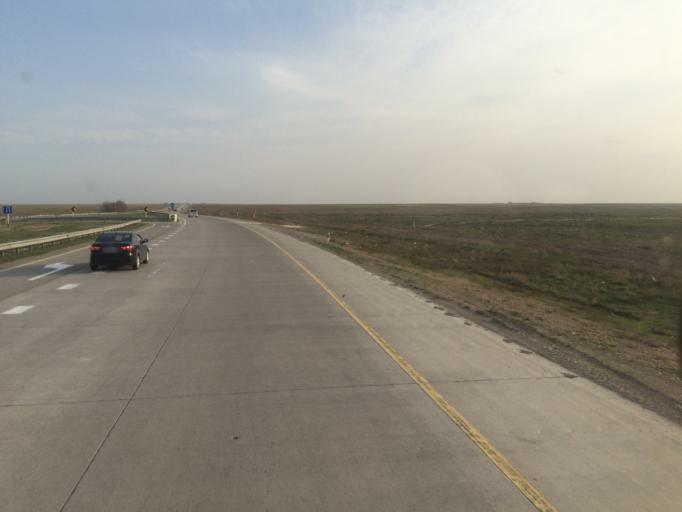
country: KZ
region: Ongtustik Qazaqstan
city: Temirlanovka
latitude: 42.7719
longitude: 69.2062
